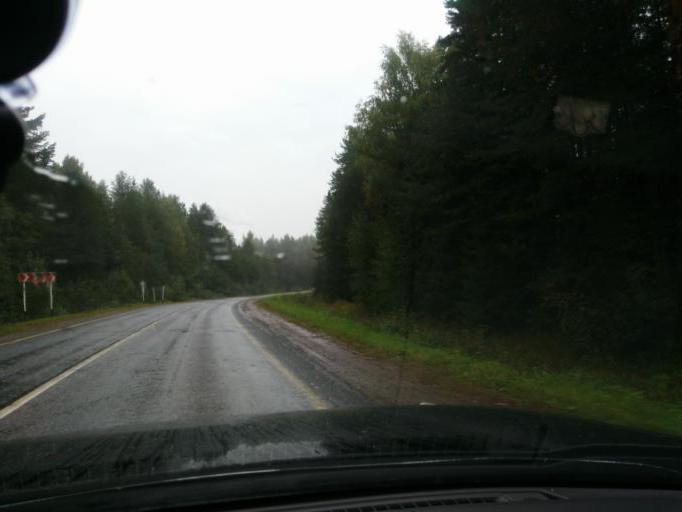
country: RU
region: Perm
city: Yugo-Kamskiy
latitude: 57.5617
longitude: 55.6793
